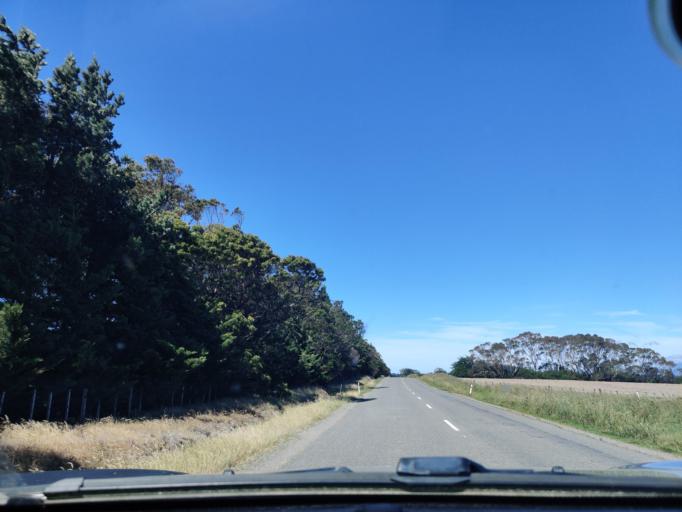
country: NZ
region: Wellington
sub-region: South Wairarapa District
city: Waipawa
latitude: -41.2110
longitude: 175.3647
